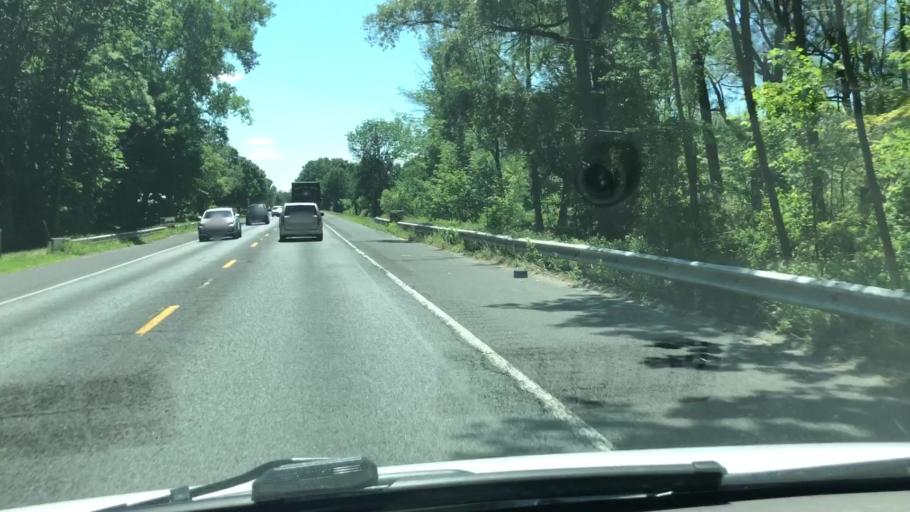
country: US
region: Massachusetts
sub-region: Berkshire County
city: Lanesborough
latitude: 42.5250
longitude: -73.1918
